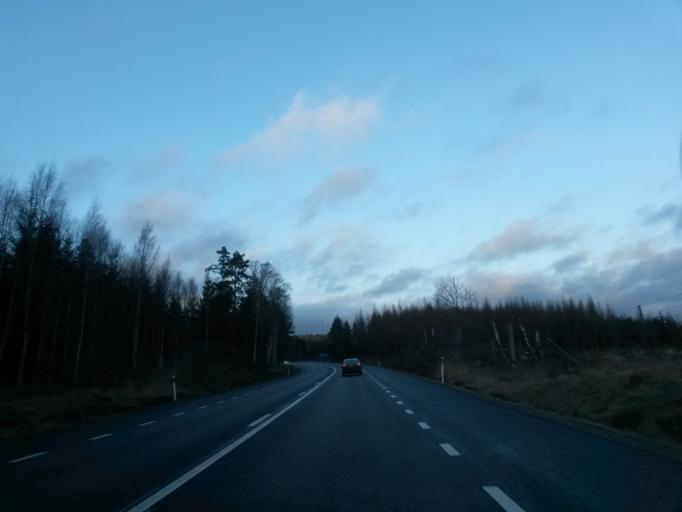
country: SE
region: Halland
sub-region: Halmstads Kommun
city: Oskarstrom
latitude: 56.7838
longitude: 12.9576
